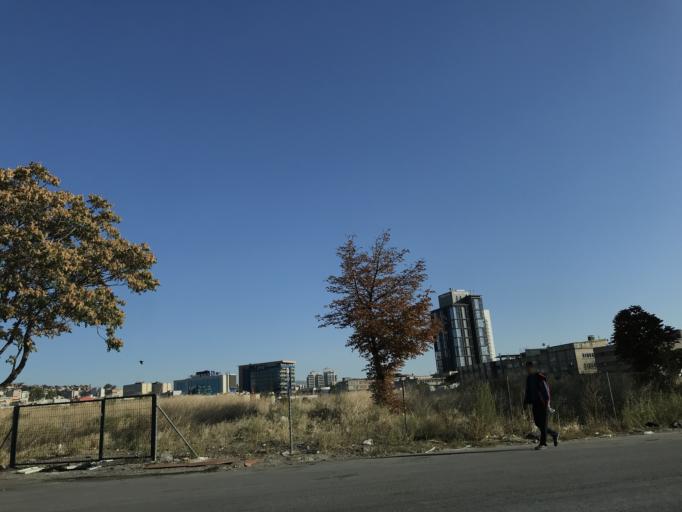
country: TR
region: Ankara
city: Ankara
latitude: 39.9491
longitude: 32.8446
